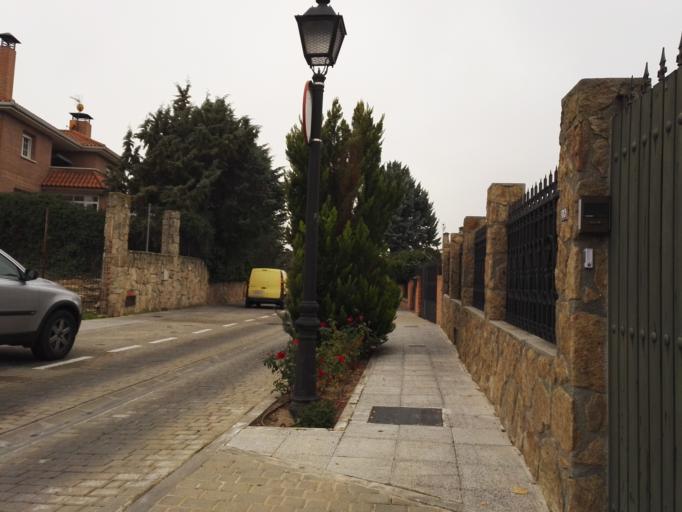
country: ES
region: Madrid
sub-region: Provincia de Madrid
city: Arroyomolinos
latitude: 40.2684
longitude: -3.9230
